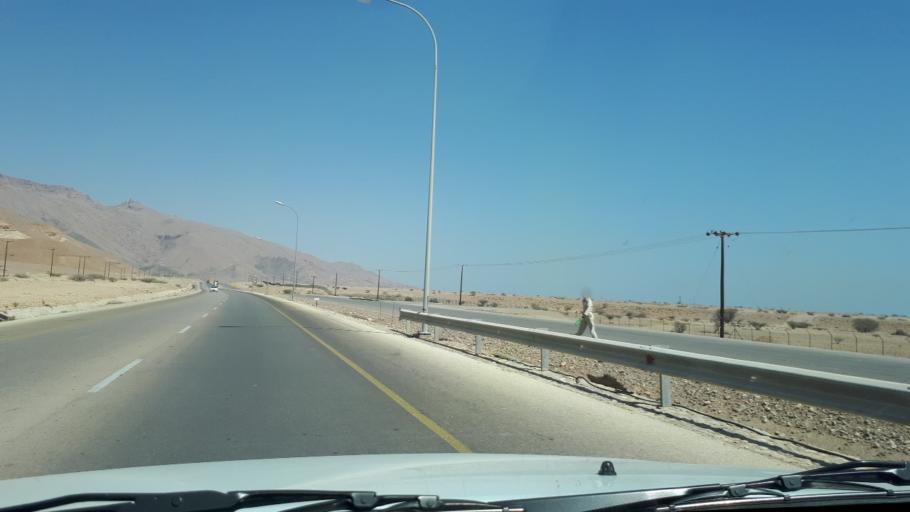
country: OM
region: Ash Sharqiyah
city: Sur
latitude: 22.6198
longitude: 59.4197
